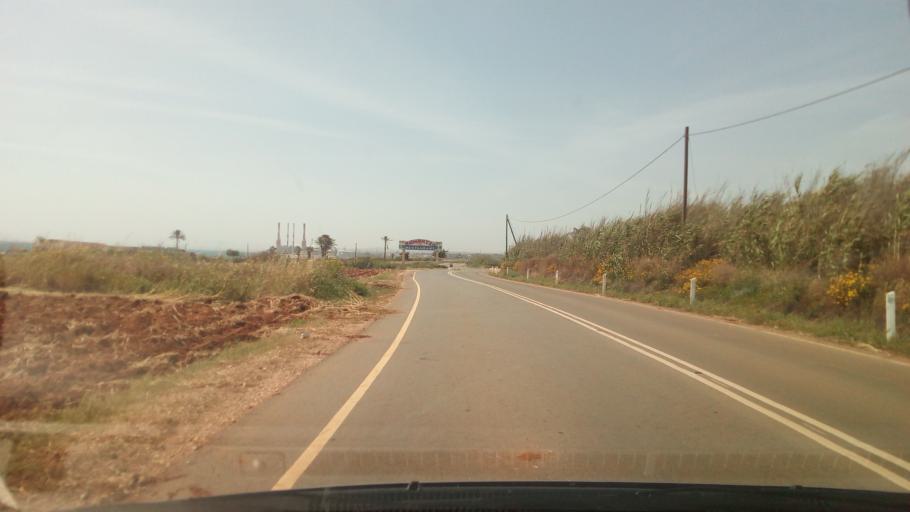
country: CY
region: Larnaka
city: Xylotymbou
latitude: 34.9805
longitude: 33.7714
